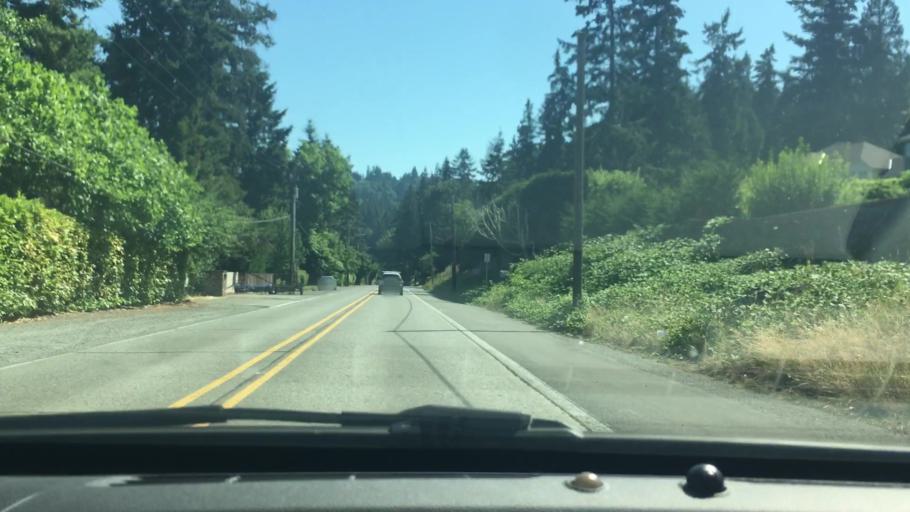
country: US
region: Washington
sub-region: King County
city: West Lake Sammamish
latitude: 47.5834
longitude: -122.1118
